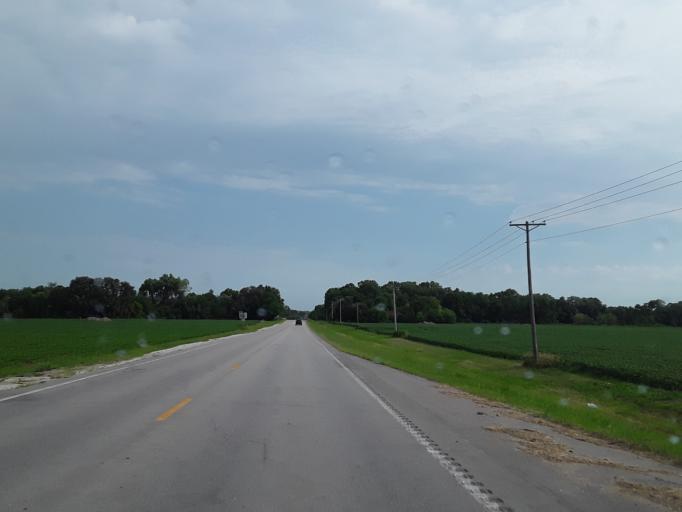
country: US
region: Nebraska
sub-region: Saunders County
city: Ashland
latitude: 41.0578
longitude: -96.3680
